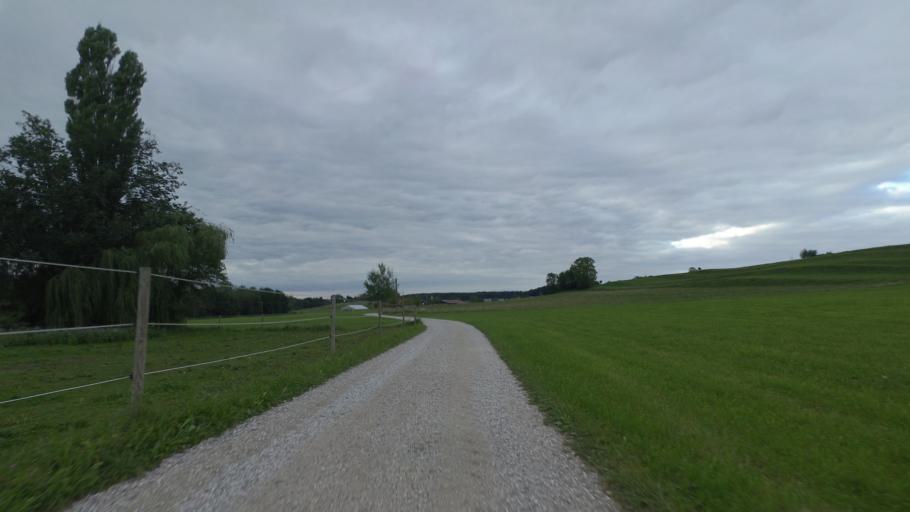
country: DE
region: Bavaria
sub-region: Upper Bavaria
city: Nussdorf
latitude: 47.9080
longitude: 12.5688
